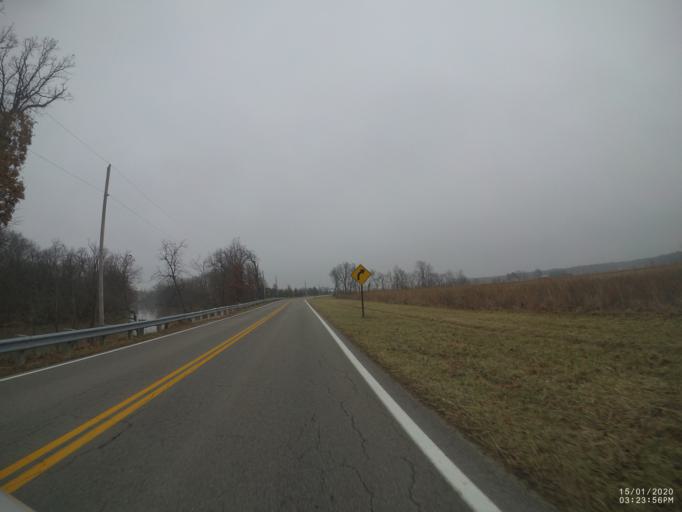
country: US
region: Ohio
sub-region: Sandusky County
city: Woodville
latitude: 41.4275
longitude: -83.4089
